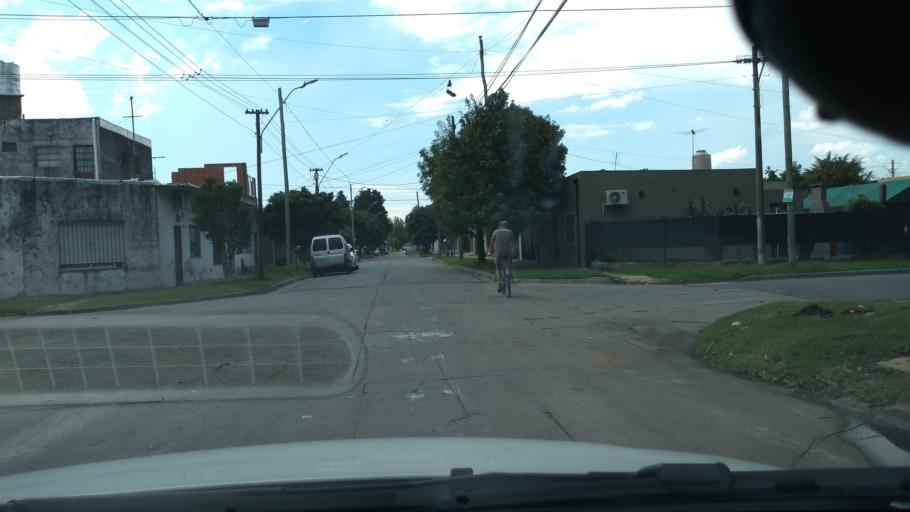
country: AR
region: Buenos Aires
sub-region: Partido de Moron
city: Moron
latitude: -34.6676
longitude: -58.6076
